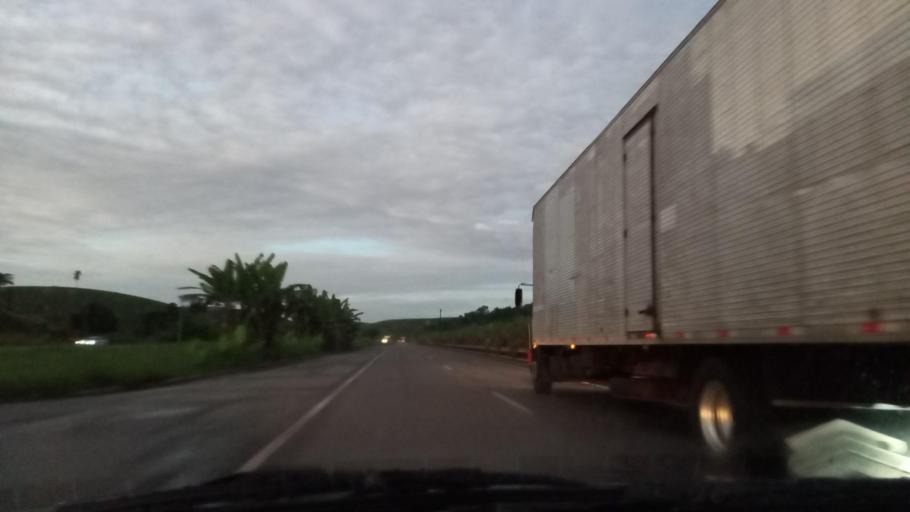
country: BR
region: Pernambuco
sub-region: Ribeirao
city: Ribeirao
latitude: -8.4330
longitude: -35.3263
